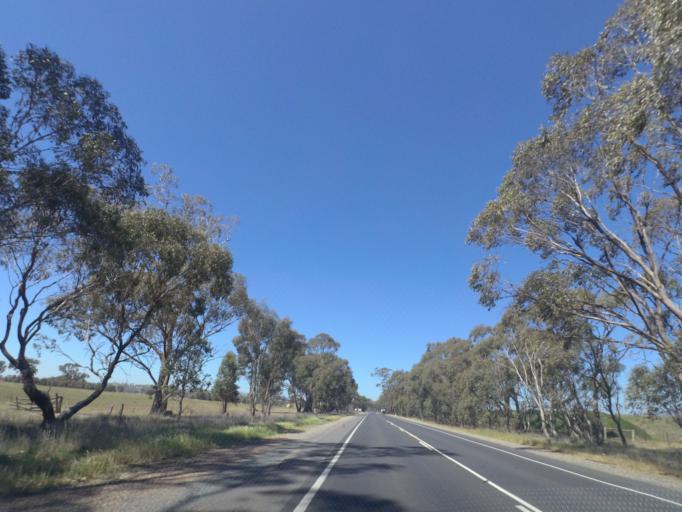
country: AU
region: Victoria
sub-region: Murrindindi
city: Kinglake West
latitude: -37.0296
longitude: 145.0784
